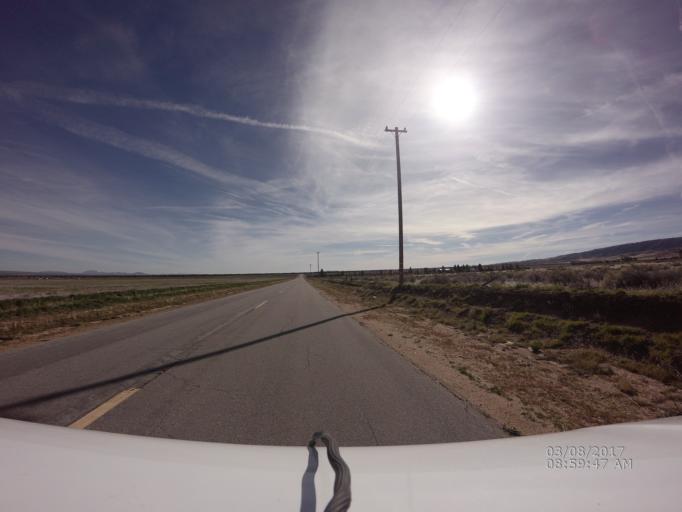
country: US
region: California
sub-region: Los Angeles County
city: Green Valley
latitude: 34.7609
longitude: -118.5262
